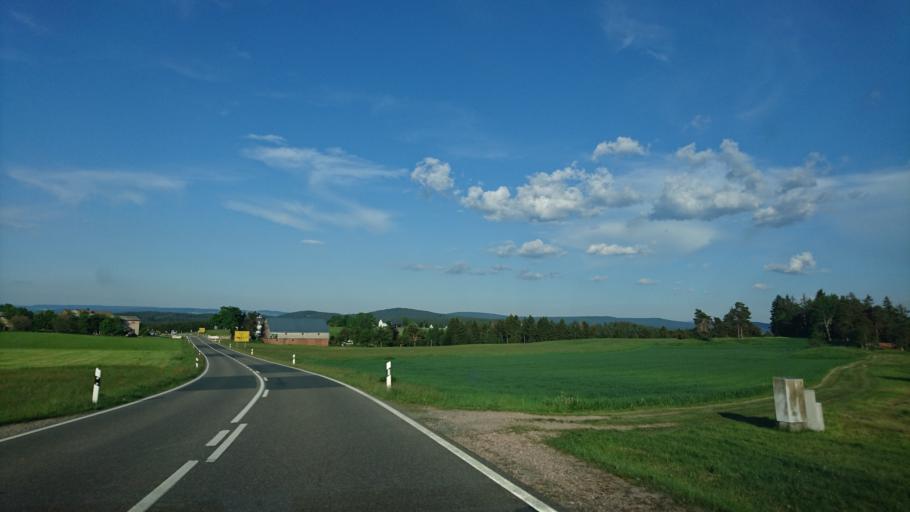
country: DE
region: Saxony
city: Stutzengrun
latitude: 50.5430
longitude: 12.5497
